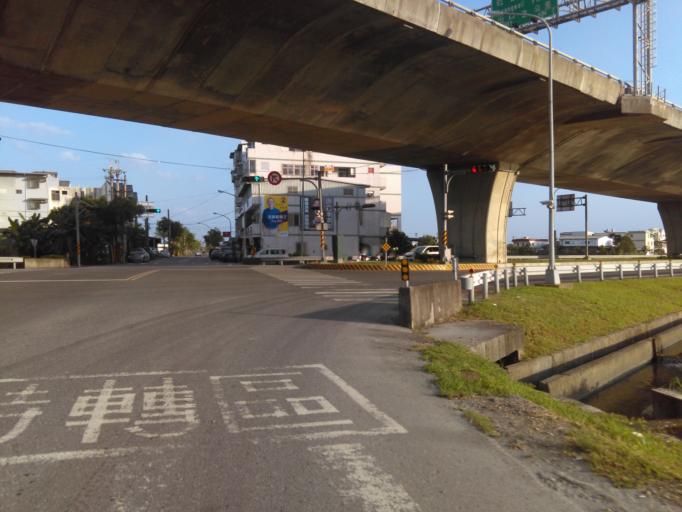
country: TW
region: Taiwan
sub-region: Yilan
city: Yilan
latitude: 24.8009
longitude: 121.7823
